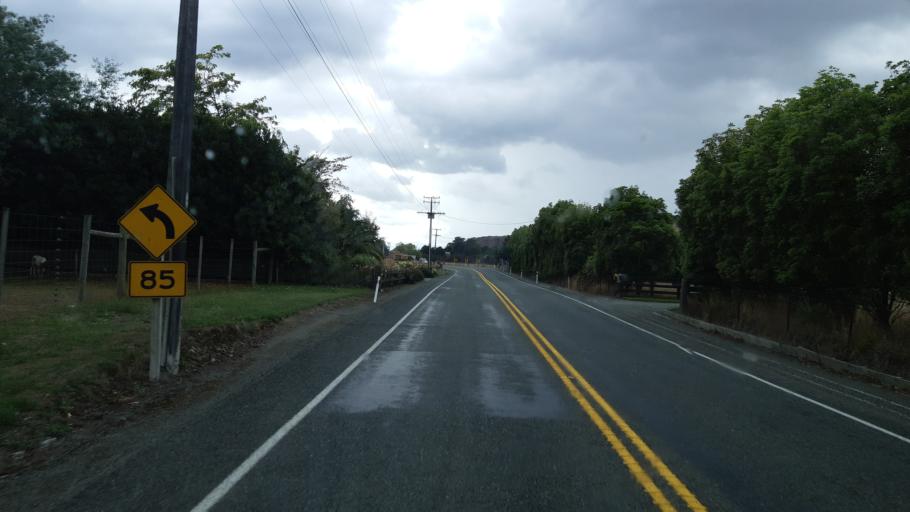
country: NZ
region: Tasman
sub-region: Tasman District
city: Wakefield
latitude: -41.4245
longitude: 173.0001
